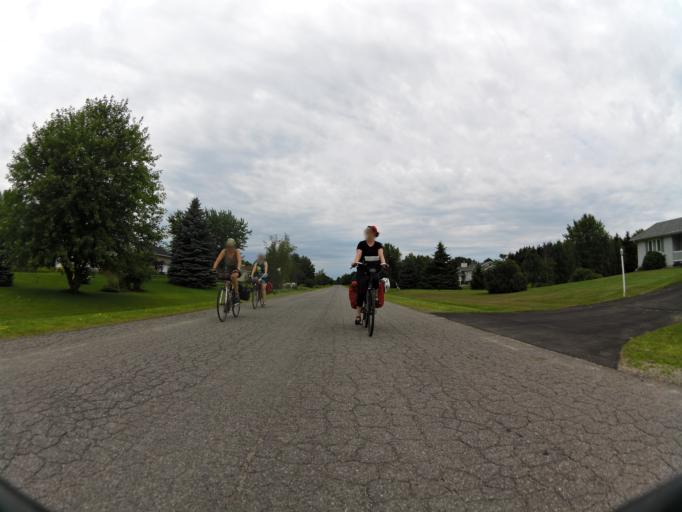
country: CA
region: Ontario
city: Bells Corners
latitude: 45.0233
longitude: -75.6924
